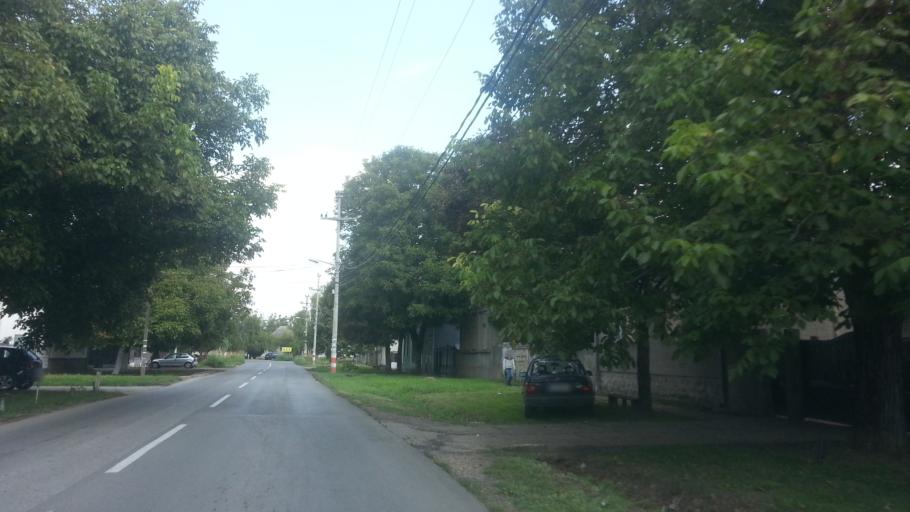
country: RS
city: Novi Banovci
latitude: 44.9106
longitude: 20.2804
